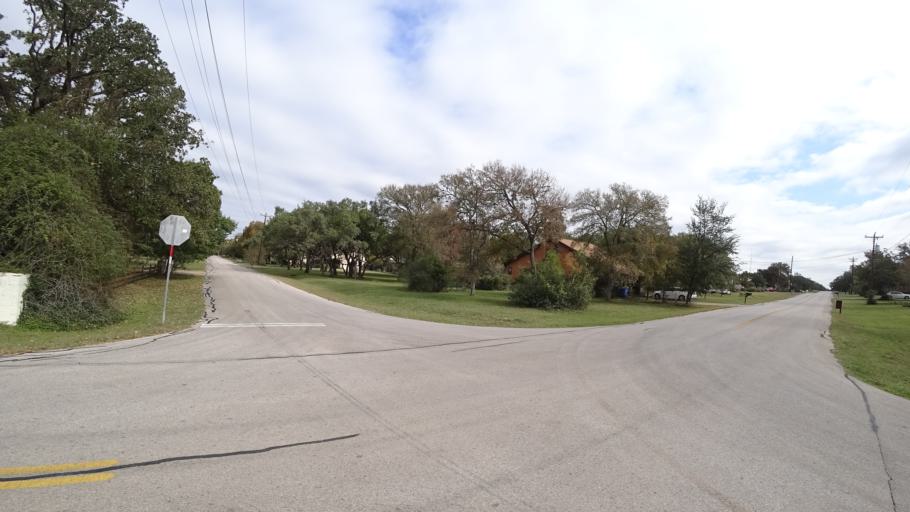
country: US
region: Texas
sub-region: Travis County
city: Shady Hollow
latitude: 30.1361
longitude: -97.8916
